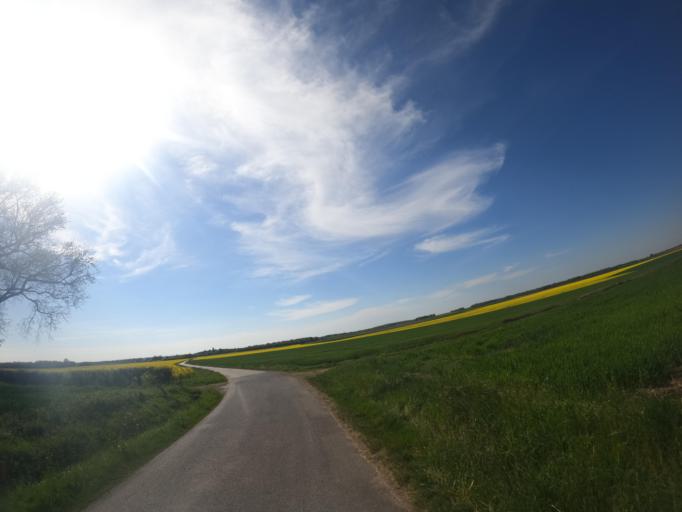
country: FR
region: Poitou-Charentes
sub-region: Departement des Deux-Sevres
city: Saint-Jean-de-Thouars
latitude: 46.9263
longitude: -0.2017
